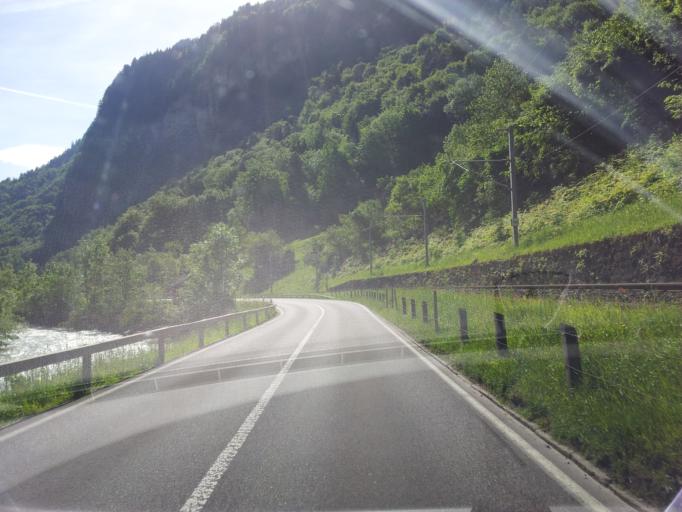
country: CH
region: Bern
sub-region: Interlaken-Oberhasli District
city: Lauterbrunnen
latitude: 46.6314
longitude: 7.9078
